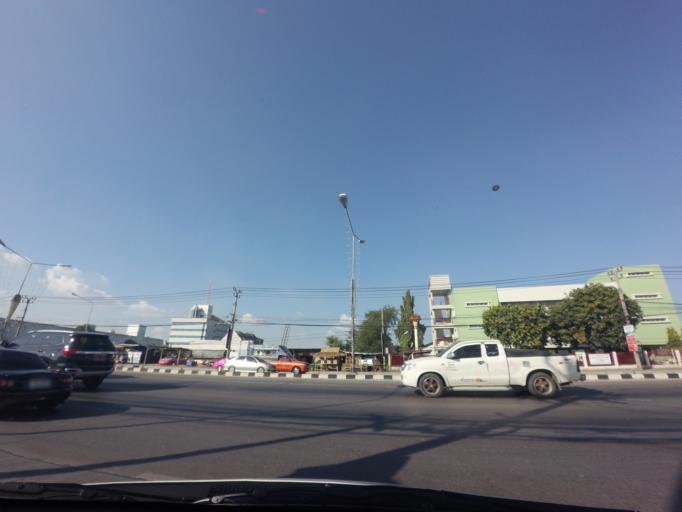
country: TH
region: Bangkok
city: Bang Na
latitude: 13.6120
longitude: 100.6669
